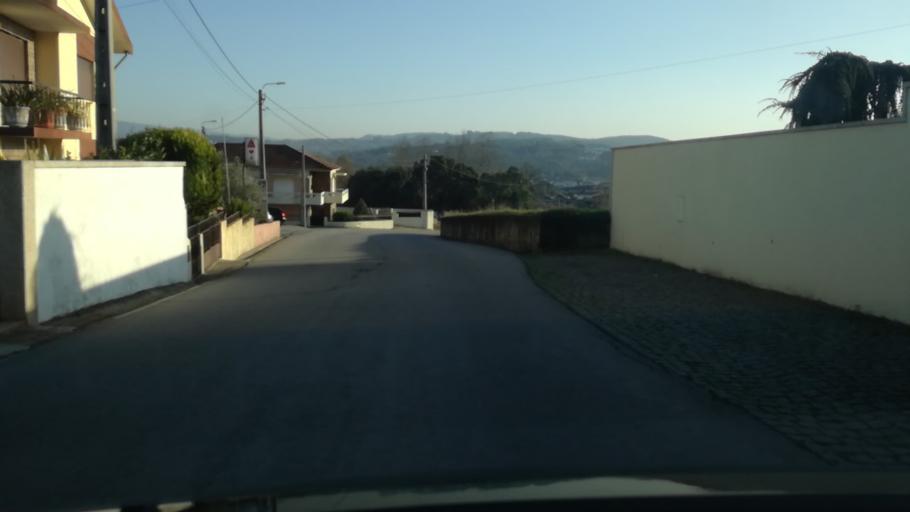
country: PT
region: Braga
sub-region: Vila Nova de Famalicao
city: Ferreiros
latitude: 41.3567
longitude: -8.5294
